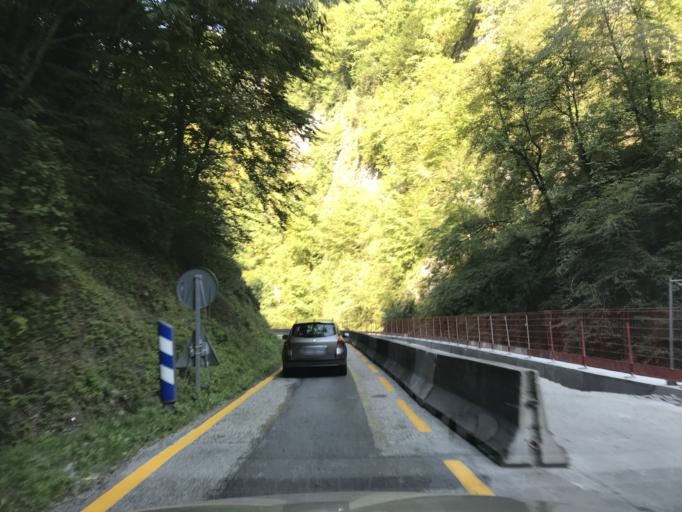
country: FR
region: Rhone-Alpes
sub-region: Departement de la Savoie
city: La Rochette
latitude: 45.4337
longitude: 6.0942
